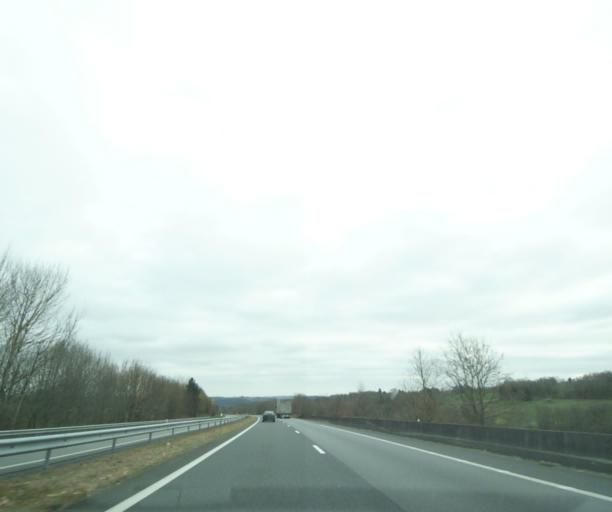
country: FR
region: Limousin
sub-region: Departement de la Correze
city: Vigeois
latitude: 45.4303
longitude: 1.5126
